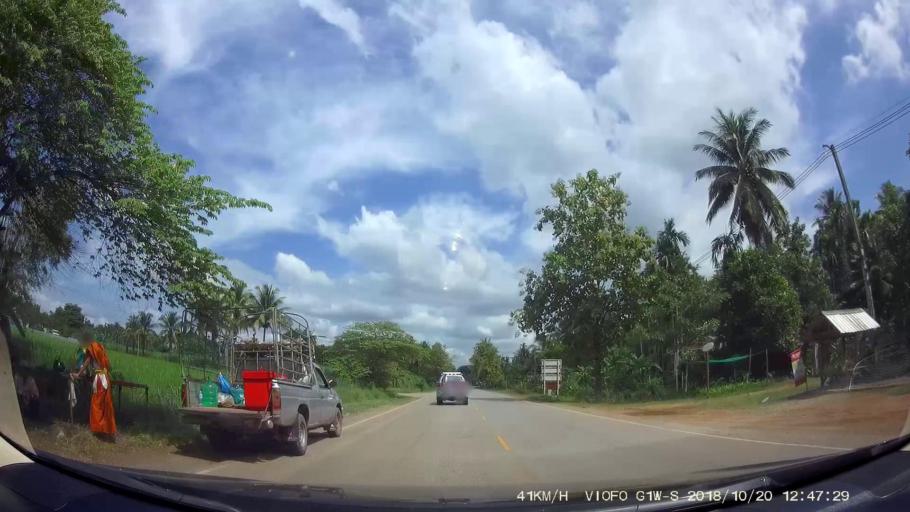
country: TH
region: Chaiyaphum
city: Khon San
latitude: 16.5339
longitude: 101.8860
